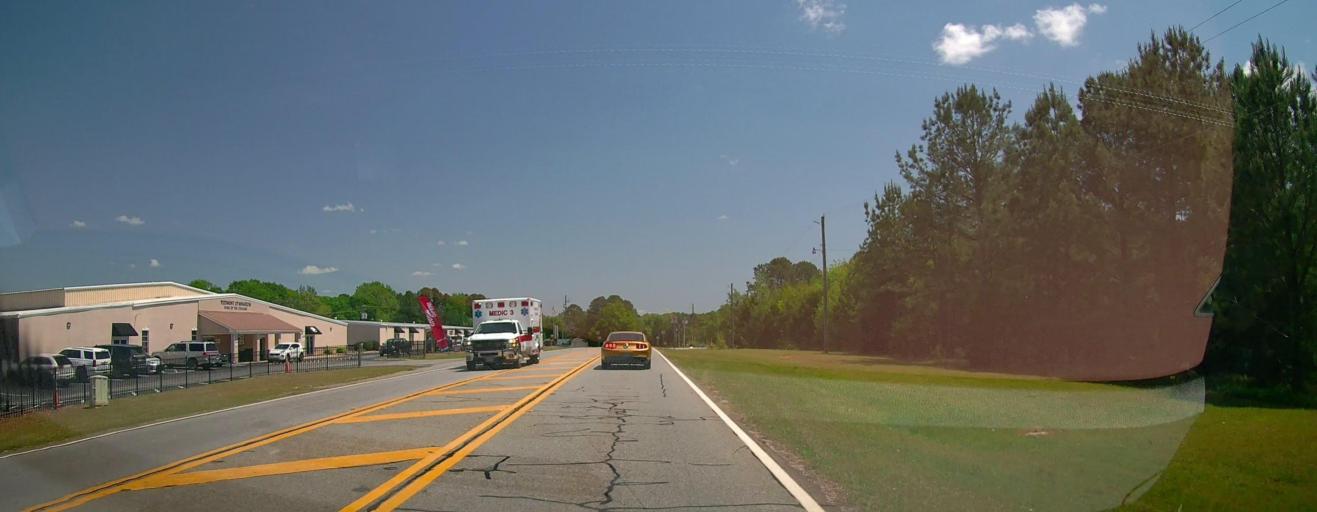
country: US
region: Georgia
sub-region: Jasper County
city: Monticello
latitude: 33.3083
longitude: -83.7000
